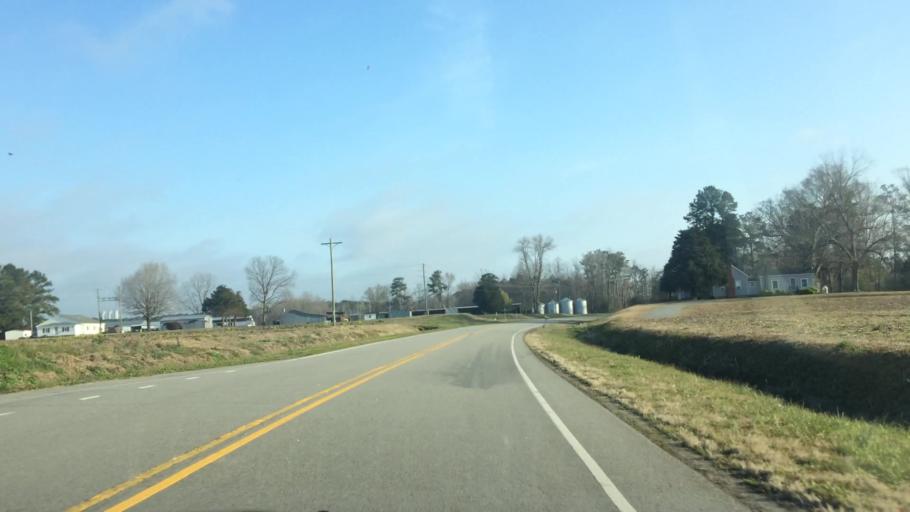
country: US
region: North Carolina
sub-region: Edgecombe County
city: Pinetops
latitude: 35.7283
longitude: -77.6356
